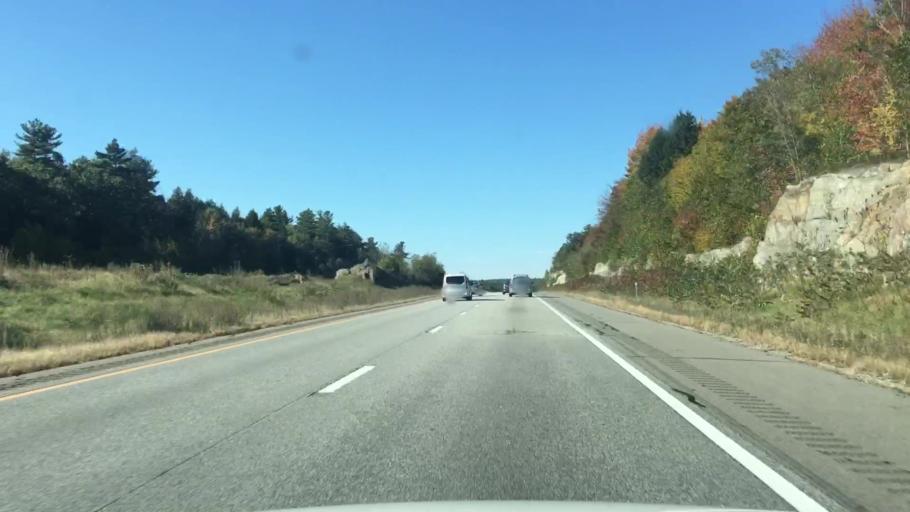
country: US
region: New Hampshire
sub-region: Rockingham County
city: Raymond
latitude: 43.0266
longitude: -71.1832
